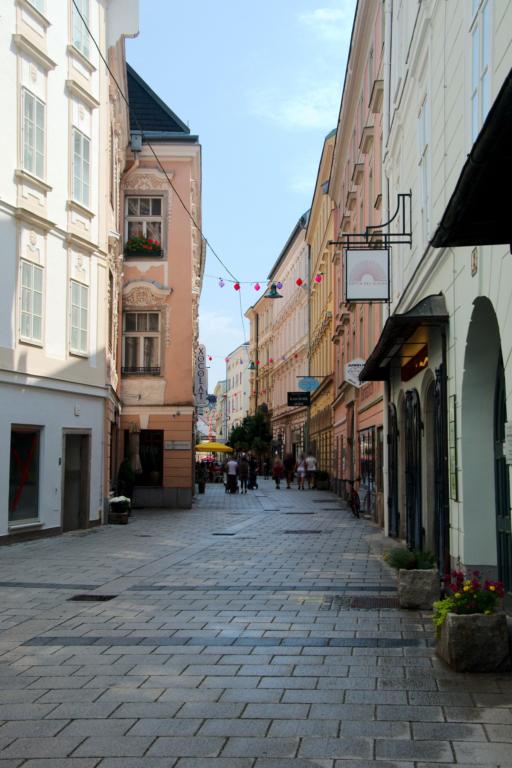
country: AT
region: Upper Austria
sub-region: Linz Stadt
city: Linz
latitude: 48.3032
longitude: 14.2859
